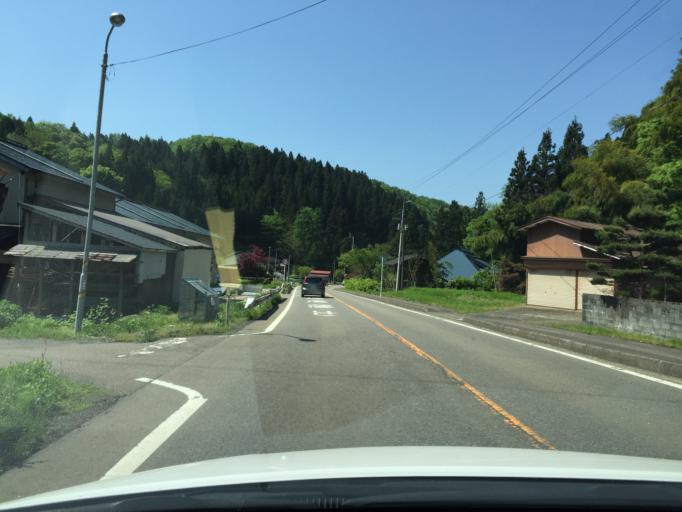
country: JP
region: Niigata
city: Kamo
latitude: 37.6370
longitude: 139.1097
